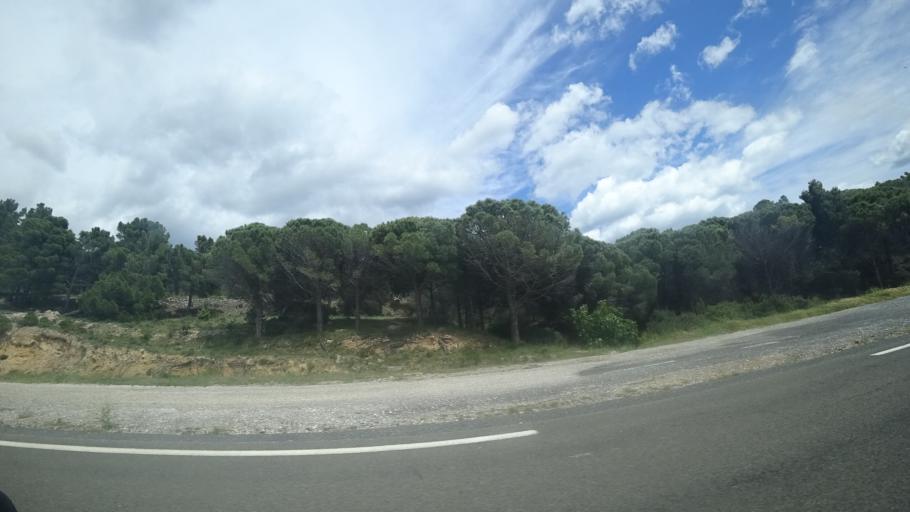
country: FR
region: Languedoc-Roussillon
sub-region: Departement de l'Aude
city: Leucate
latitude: 42.9153
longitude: 3.0214
